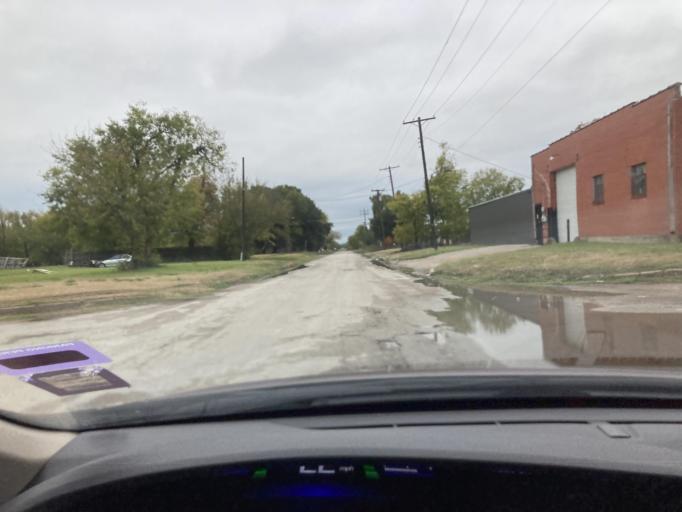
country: US
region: Texas
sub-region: Navarro County
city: Corsicana
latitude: 32.0905
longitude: -96.4595
